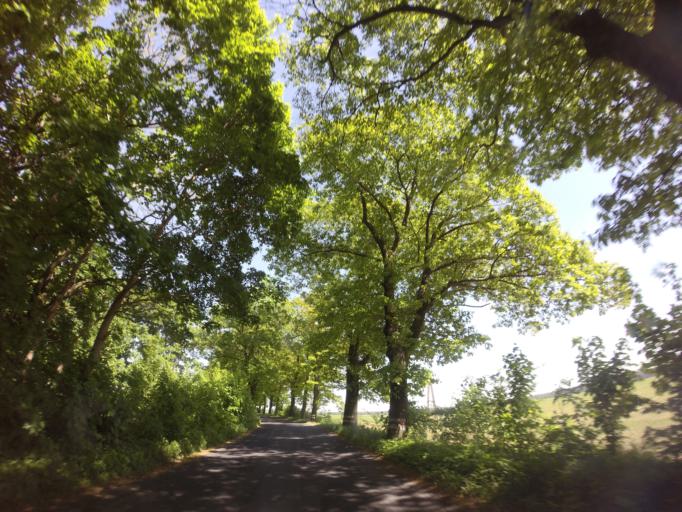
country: PL
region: West Pomeranian Voivodeship
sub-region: Powiat mysliborski
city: Nowogrodek Pomorski
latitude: 52.9140
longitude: 15.1245
